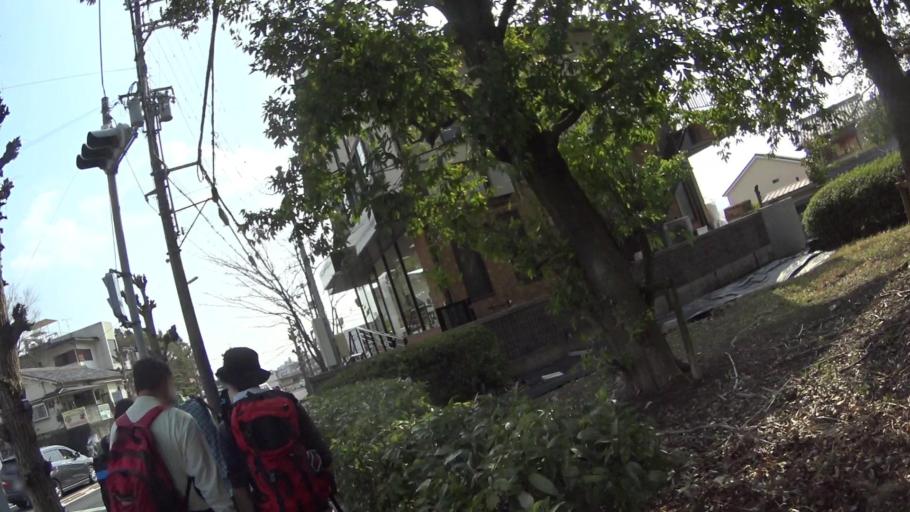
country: JP
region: Nara
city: Nara-shi
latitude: 34.6944
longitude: 135.8258
